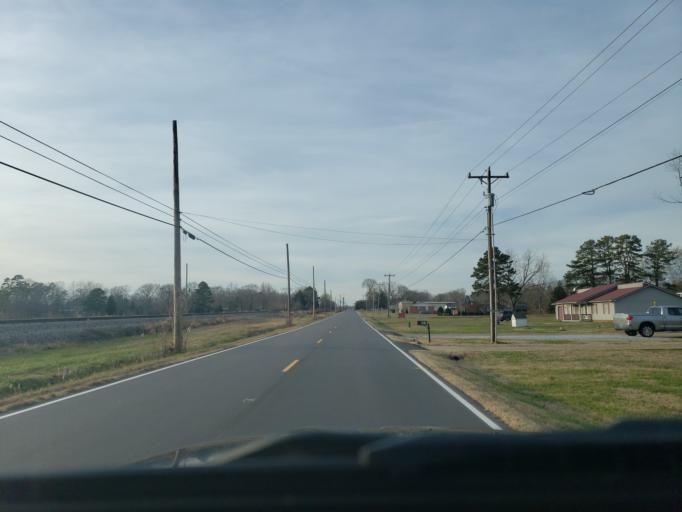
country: US
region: North Carolina
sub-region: Cleveland County
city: Boiling Springs
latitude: 35.3148
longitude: -81.7413
